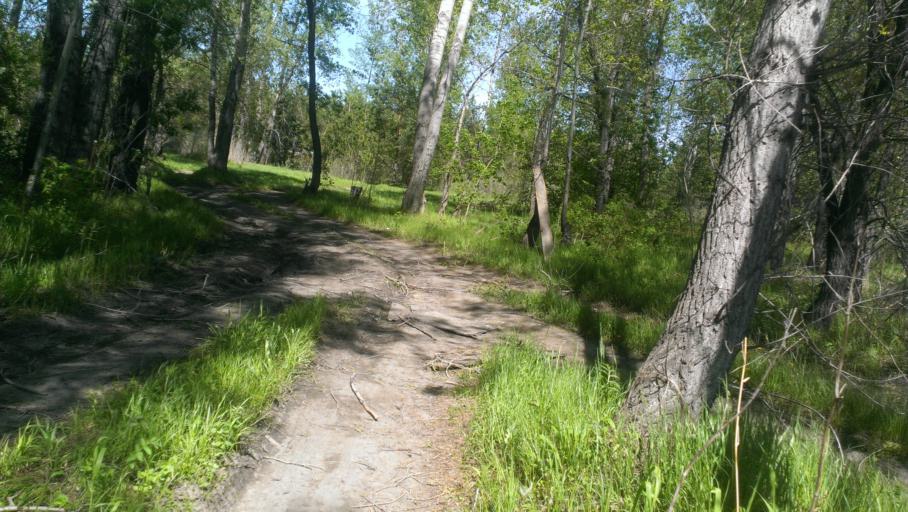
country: RU
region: Altai Krai
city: Zaton
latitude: 53.3136
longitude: 83.8536
